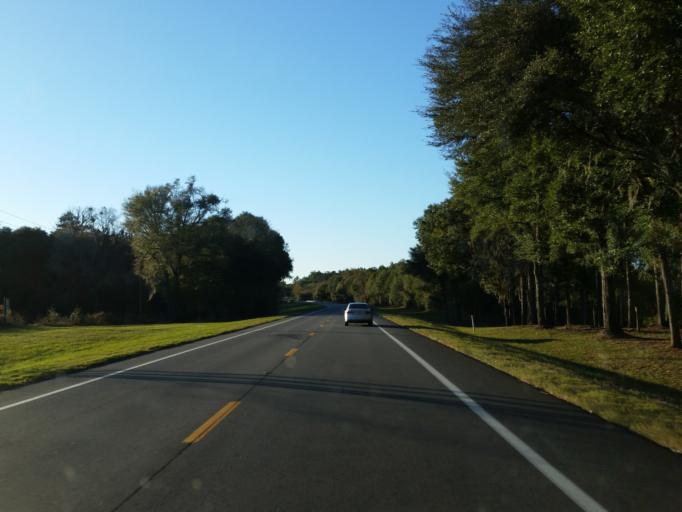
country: US
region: Florida
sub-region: Hamilton County
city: Jasper
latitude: 30.5272
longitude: -83.0328
